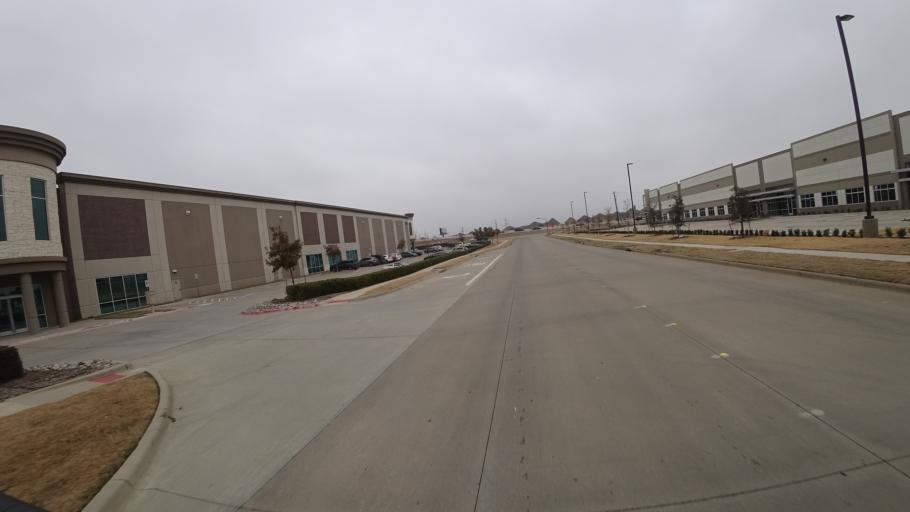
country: US
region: Texas
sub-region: Denton County
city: The Colony
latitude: 33.0606
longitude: -96.9050
